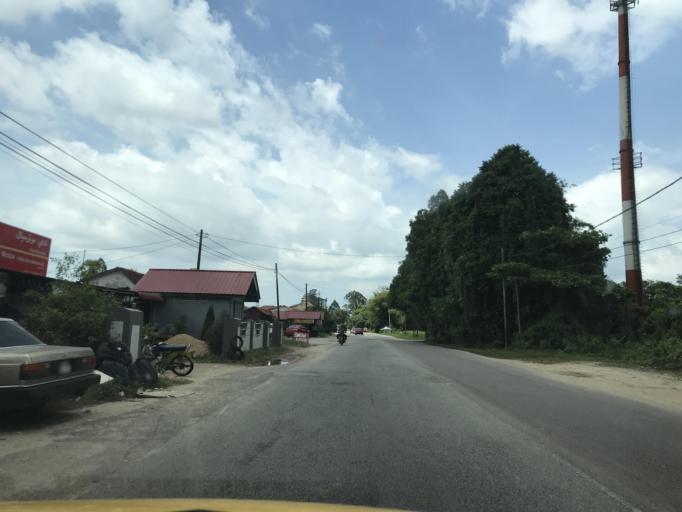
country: MY
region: Kelantan
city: Pasir Mas
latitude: 6.0502
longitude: 102.1805
